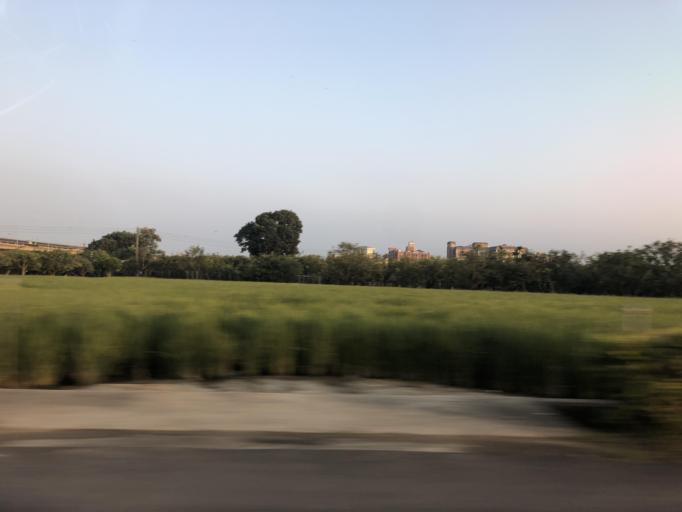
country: TW
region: Taiwan
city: Xinying
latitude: 23.1975
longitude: 120.2652
